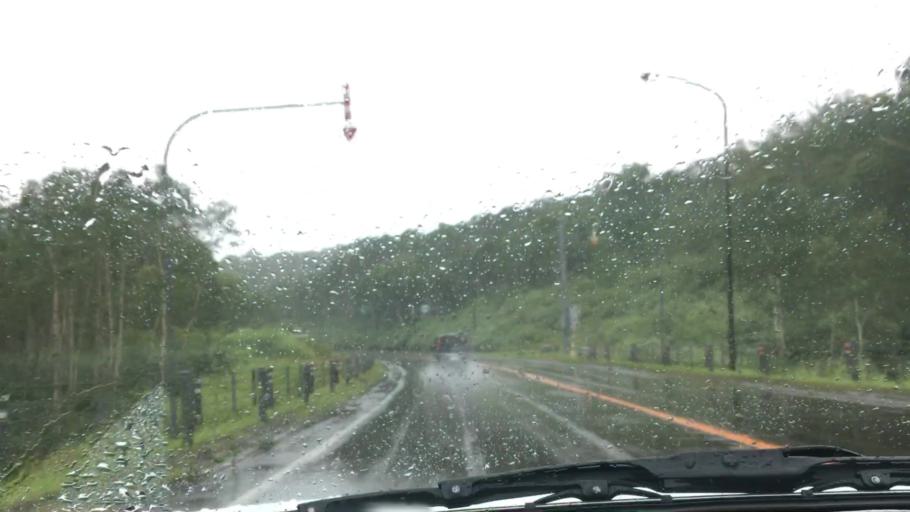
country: JP
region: Hokkaido
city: Sapporo
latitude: 42.8634
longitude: 141.1056
